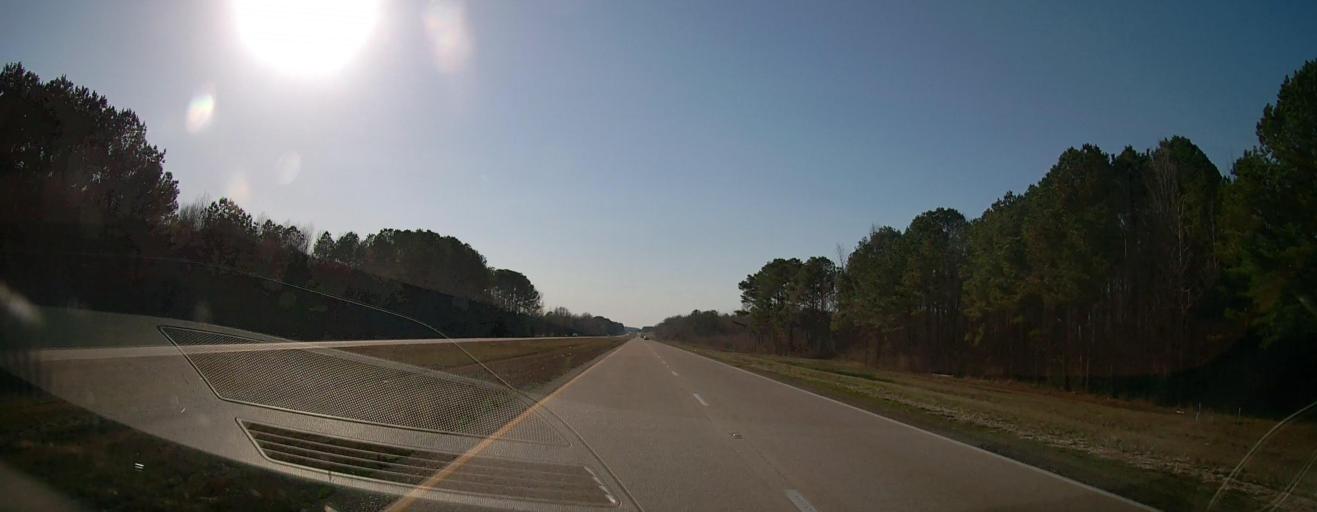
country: US
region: Mississippi
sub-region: Tishomingo County
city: Iuka
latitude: 34.8039
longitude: -88.2403
